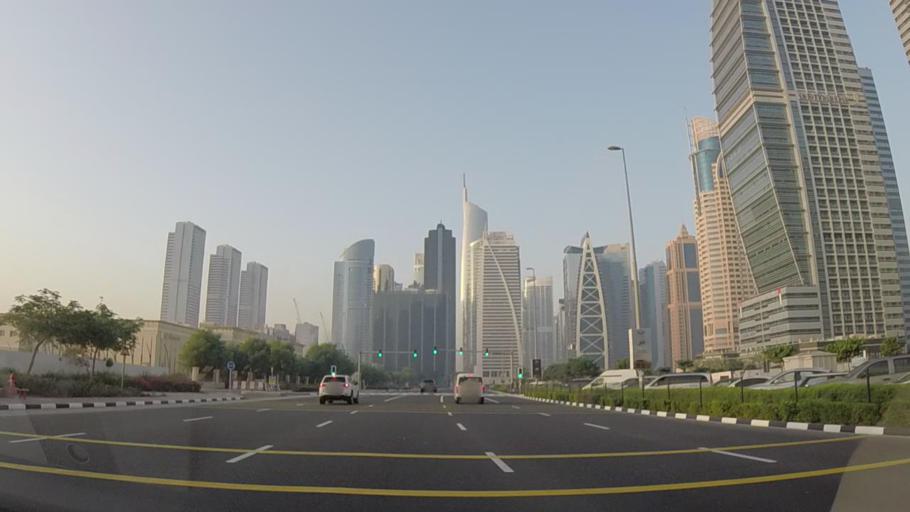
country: AE
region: Dubai
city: Dubai
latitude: 25.0753
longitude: 55.1474
